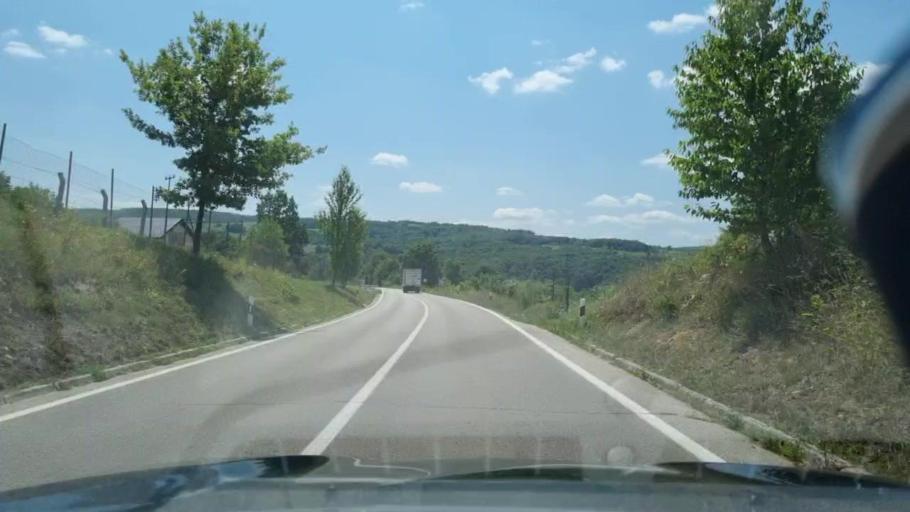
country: BA
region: Federation of Bosnia and Herzegovina
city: Peci
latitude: 44.6658
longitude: 16.7447
